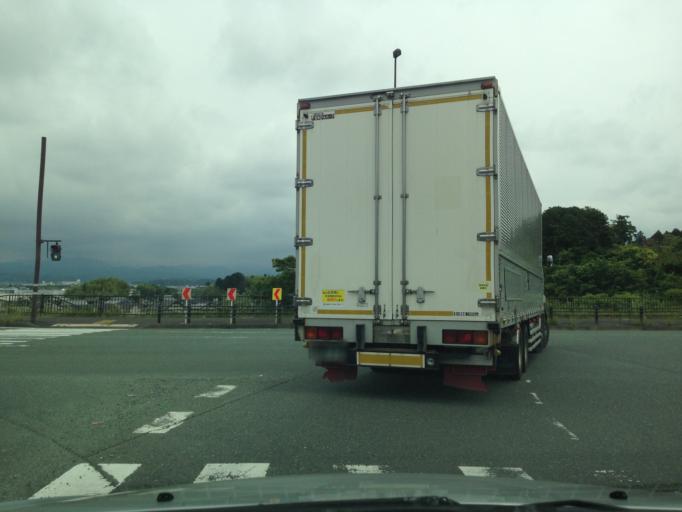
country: JP
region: Shizuoka
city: Kakegawa
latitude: 34.7516
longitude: 137.9746
